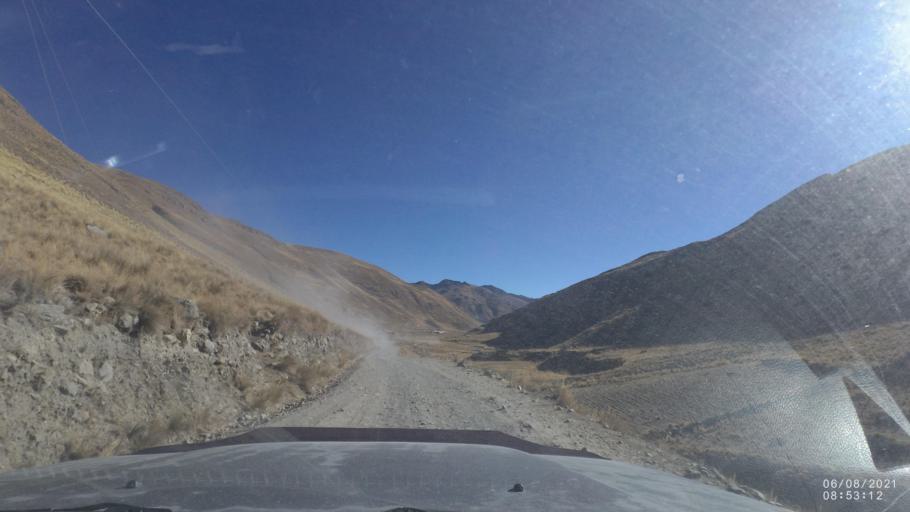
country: BO
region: Cochabamba
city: Sipe Sipe
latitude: -17.1311
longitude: -66.4397
